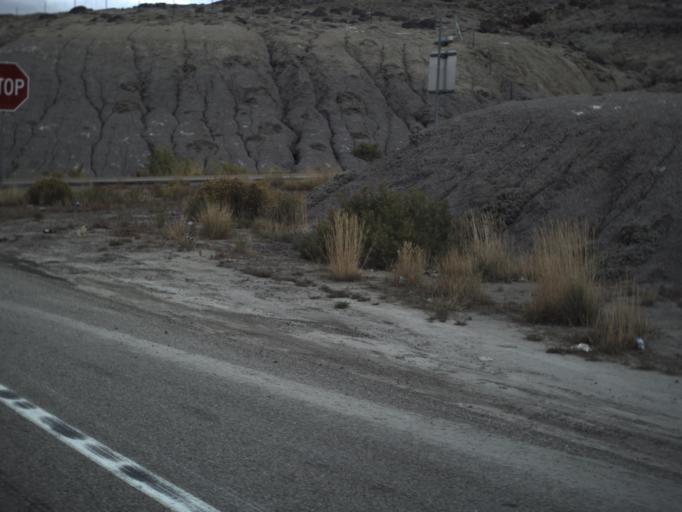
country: US
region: Utah
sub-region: Emery County
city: Ferron
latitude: 38.7652
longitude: -111.3501
